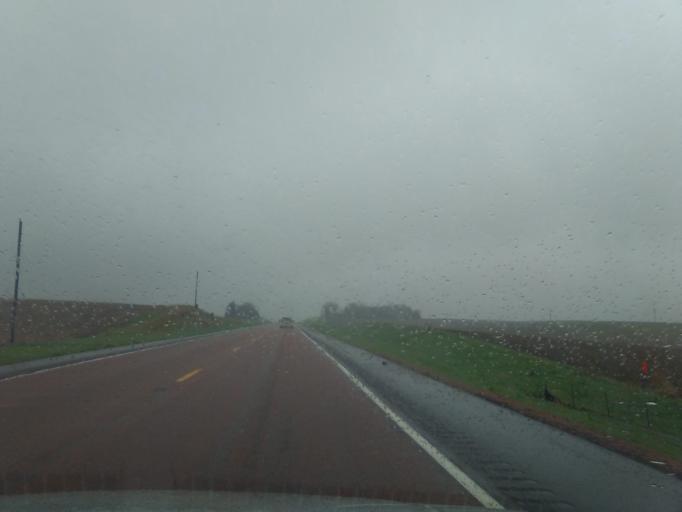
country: US
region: Nebraska
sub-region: Wayne County
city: Wayne
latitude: 42.2355
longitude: -97.1495
